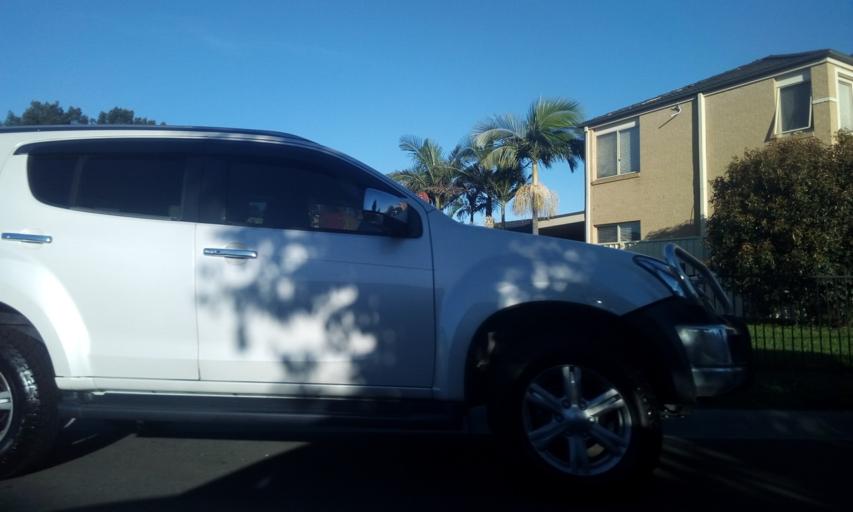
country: AU
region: New South Wales
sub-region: Wollongong
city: Dapto
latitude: -34.4879
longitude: 150.7964
